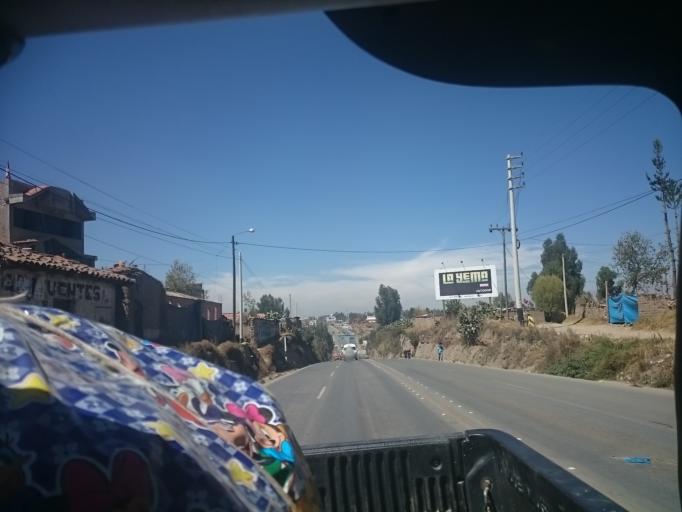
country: PE
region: Junin
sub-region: Provincia de Huancayo
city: Pilcomay
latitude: -12.0167
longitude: -75.2432
